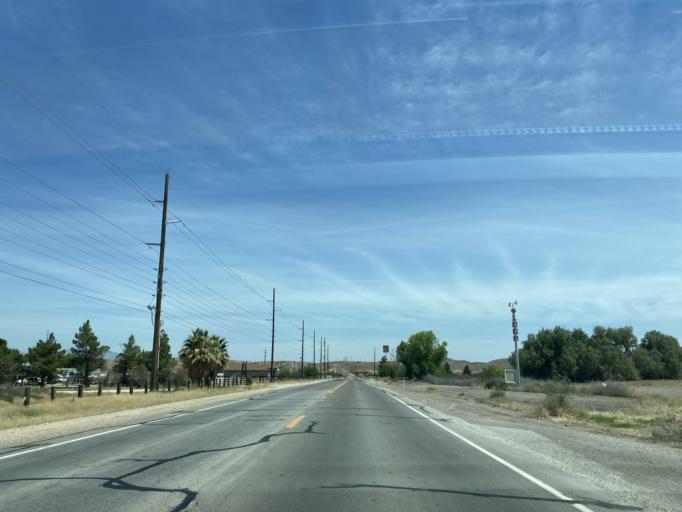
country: US
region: Nevada
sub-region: Clark County
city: Moapa Town
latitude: 36.6657
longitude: -114.5828
